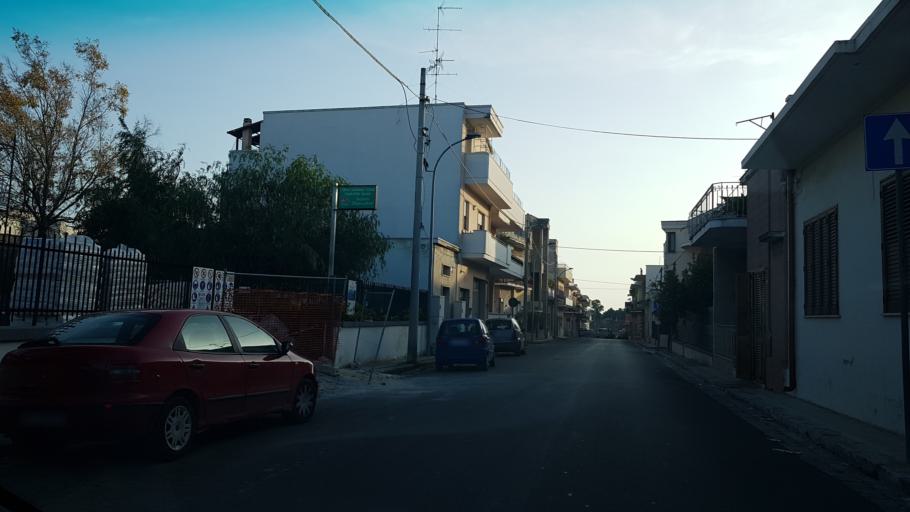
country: IT
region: Apulia
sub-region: Provincia di Lecce
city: Novoli
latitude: 40.3740
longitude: 18.0512
